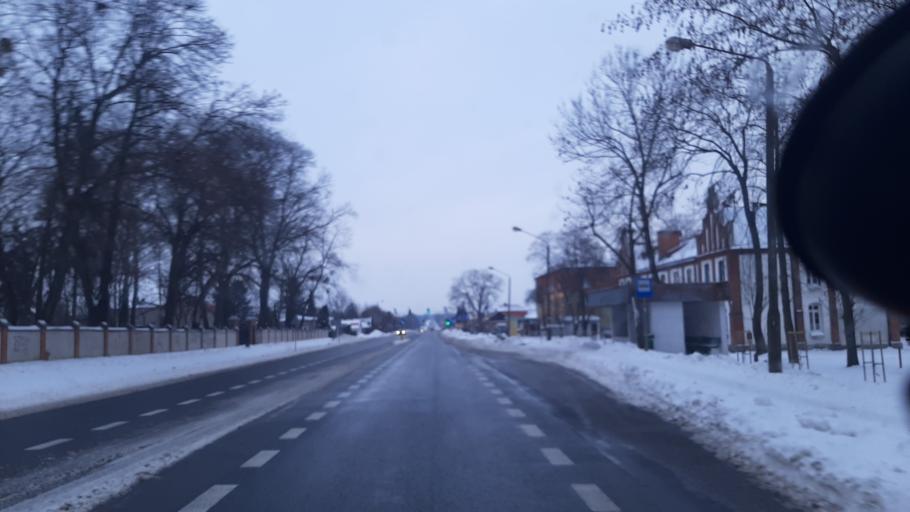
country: PL
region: Lublin Voivodeship
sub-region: Powiat lubelski
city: Garbow
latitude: 51.3644
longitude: 22.2975
